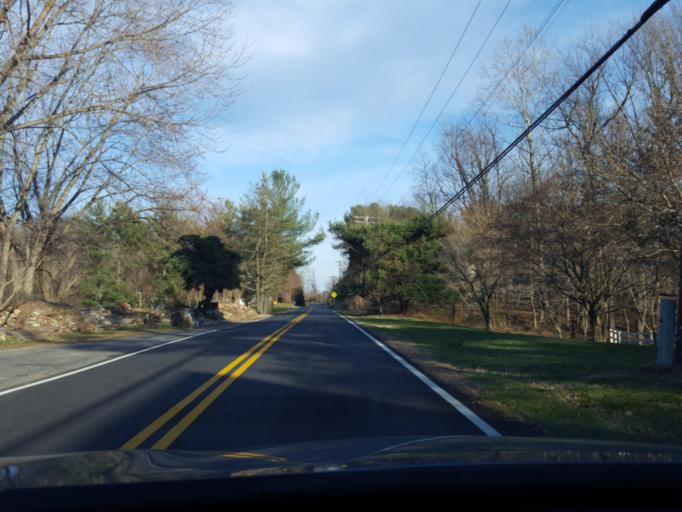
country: US
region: Maryland
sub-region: Anne Arundel County
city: Deale
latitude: 38.7543
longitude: -76.5687
